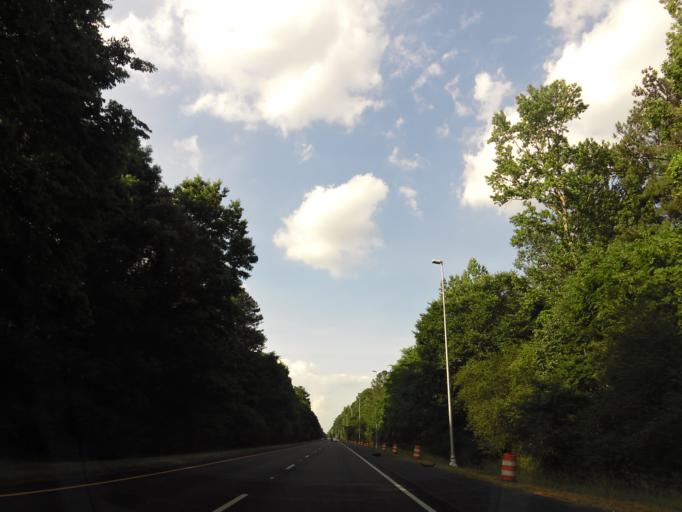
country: US
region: Alabama
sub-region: Jefferson County
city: Trussville
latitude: 33.6151
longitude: -86.6384
